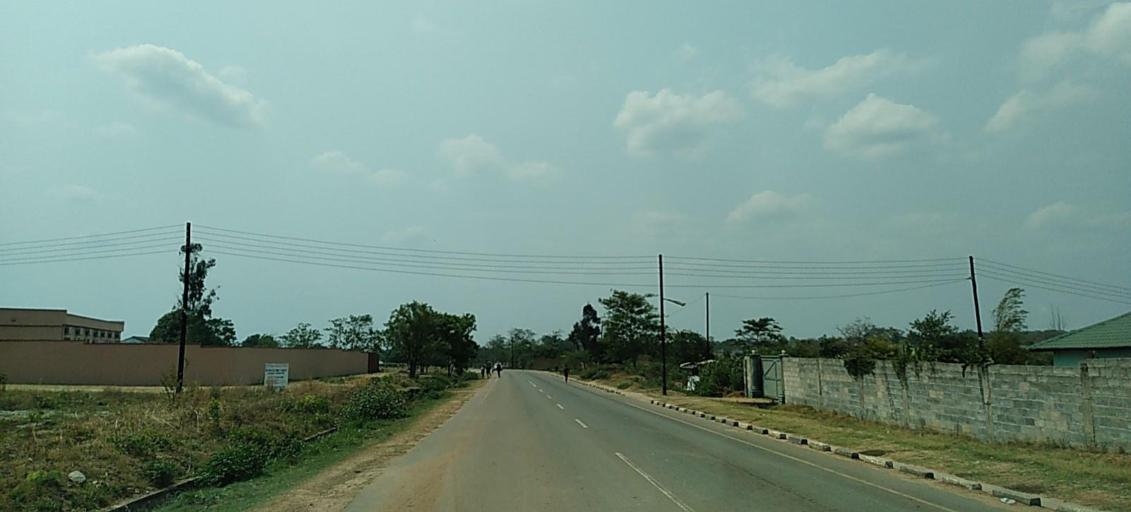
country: ZM
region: Copperbelt
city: Chambishi
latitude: -12.6381
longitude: 28.0593
